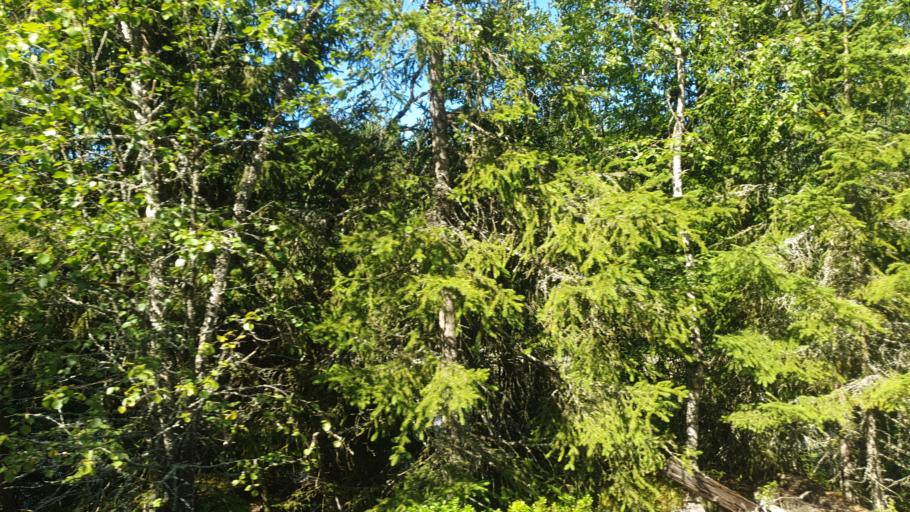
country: NO
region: Sor-Trondelag
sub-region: Orkdal
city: Orkanger
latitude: 63.1844
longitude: 9.7716
